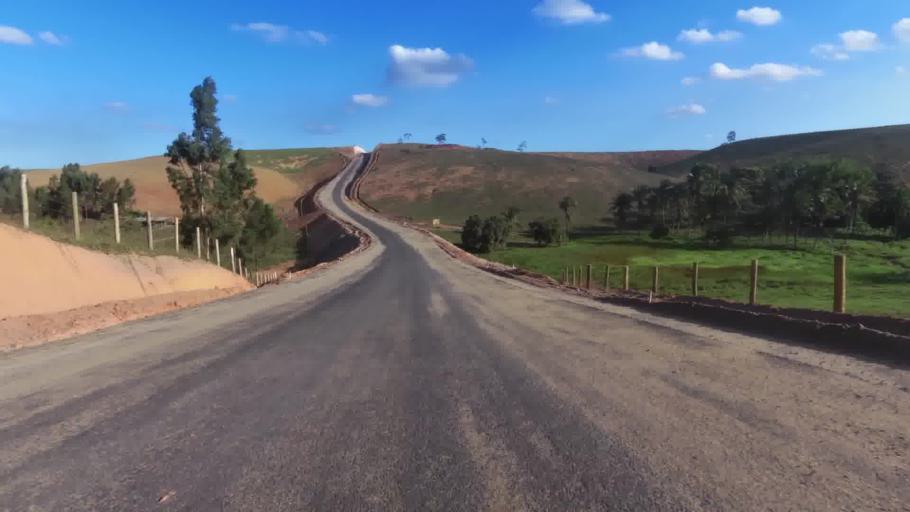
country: BR
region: Espirito Santo
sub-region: Marataizes
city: Marataizes
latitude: -21.1132
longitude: -41.0480
